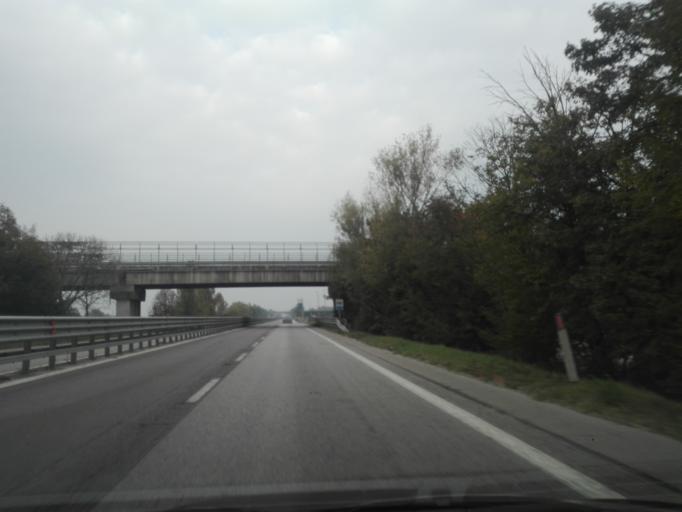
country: IT
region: Veneto
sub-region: Provincia di Verona
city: Spinimbecco
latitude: 45.1378
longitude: 11.3608
